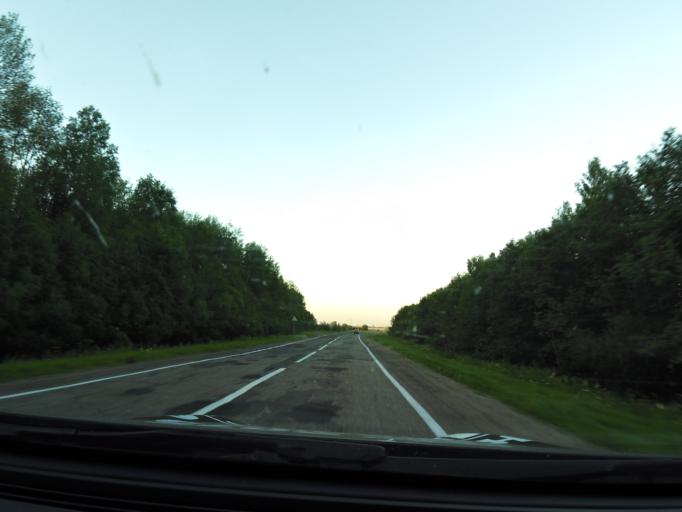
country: RU
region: Jaroslavl
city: Lyubim
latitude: 58.3567
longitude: 40.6431
